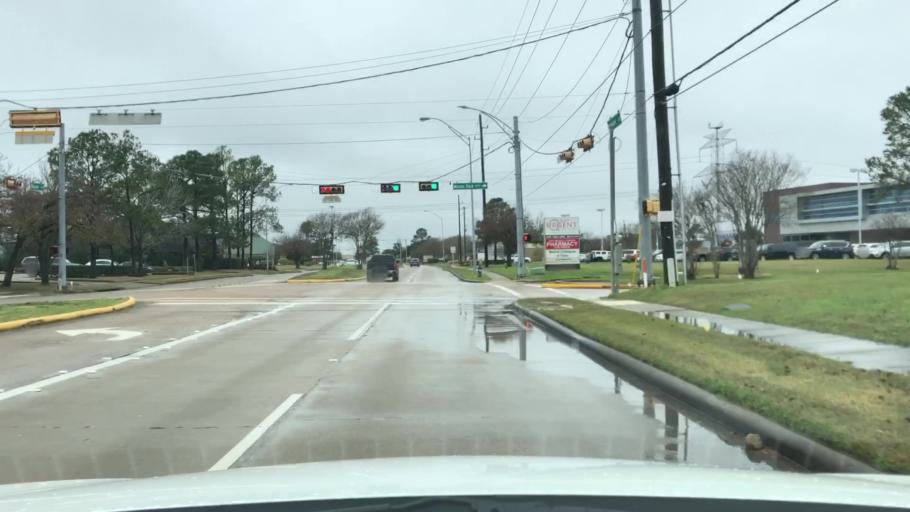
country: US
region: Texas
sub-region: Fort Bend County
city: Cinco Ranch
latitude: 29.7750
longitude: -95.7446
